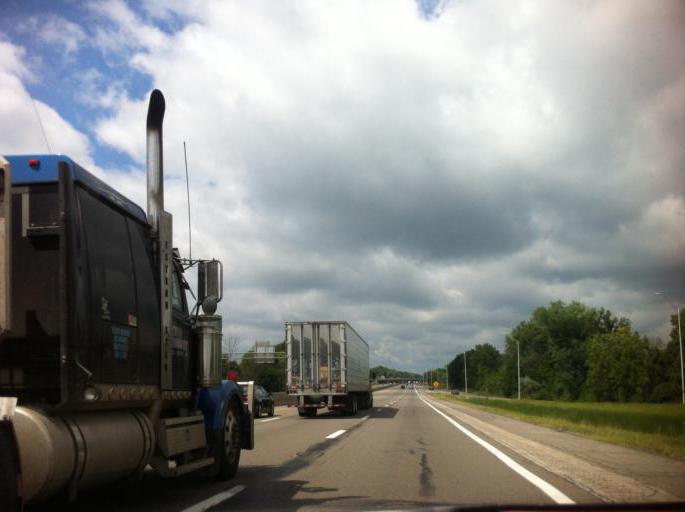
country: US
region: Ohio
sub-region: Lorain County
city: North Ridgeville
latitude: 41.3793
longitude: -81.9953
